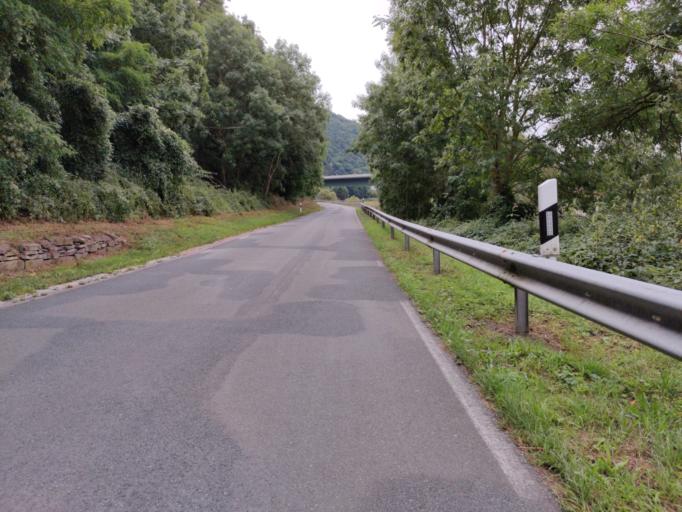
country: DE
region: Lower Saxony
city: Bodenwerder
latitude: 51.9863
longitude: 9.5183
